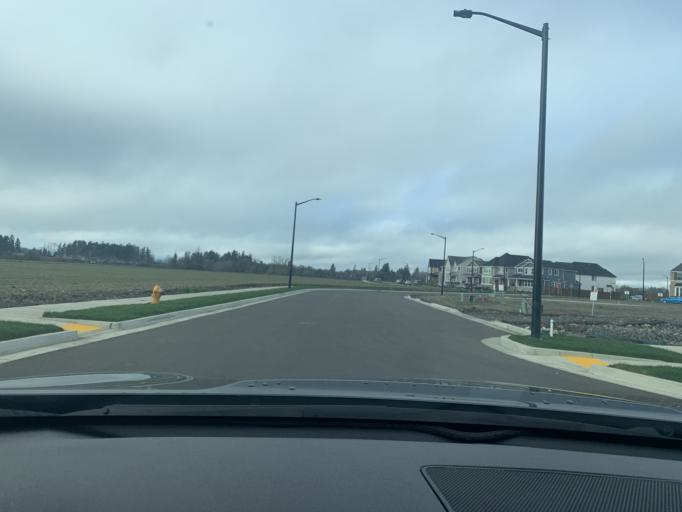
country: US
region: Oregon
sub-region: Washington County
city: North Plains
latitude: 45.5936
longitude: -122.9764
